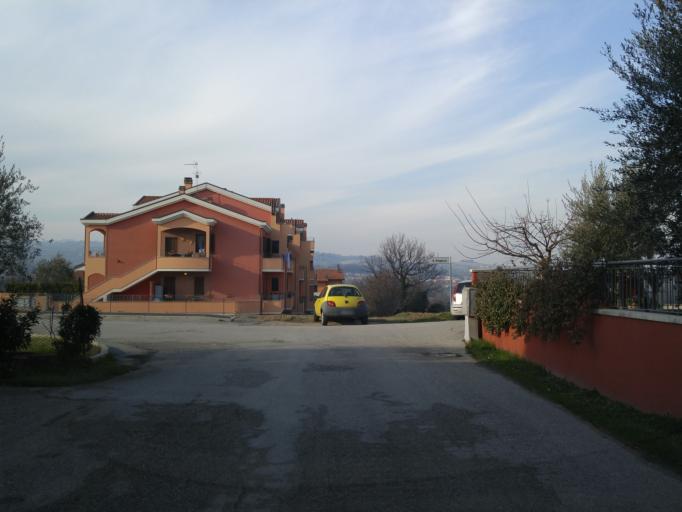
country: IT
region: The Marches
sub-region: Provincia di Pesaro e Urbino
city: Villanova
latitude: 43.7432
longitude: 12.9359
